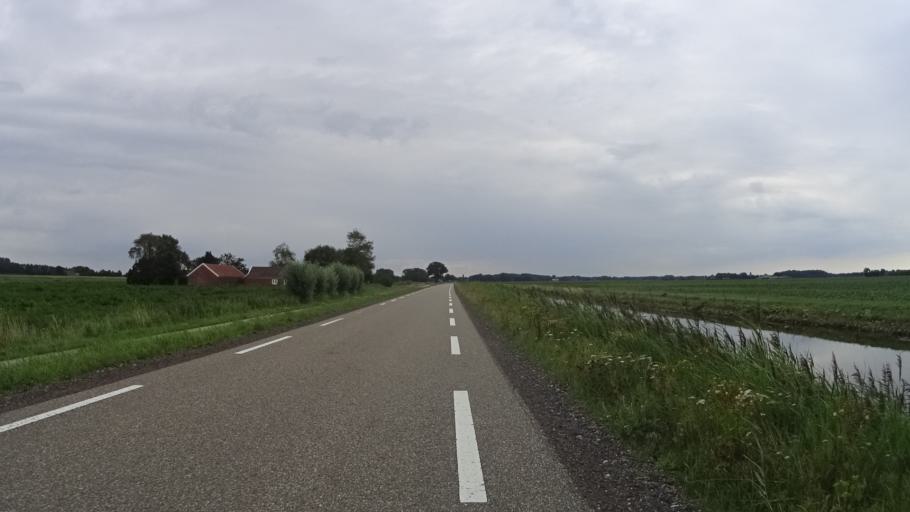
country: NL
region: Groningen
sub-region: Gemeente Slochteren
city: Slochteren
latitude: 53.2285
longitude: 6.7708
